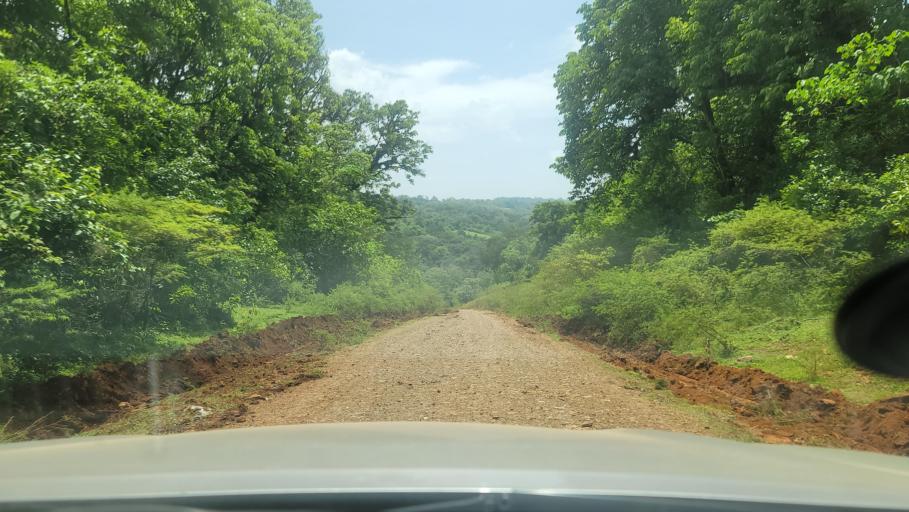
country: ET
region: Southern Nations, Nationalities, and People's Region
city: Bonga
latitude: 7.6833
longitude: 36.2395
